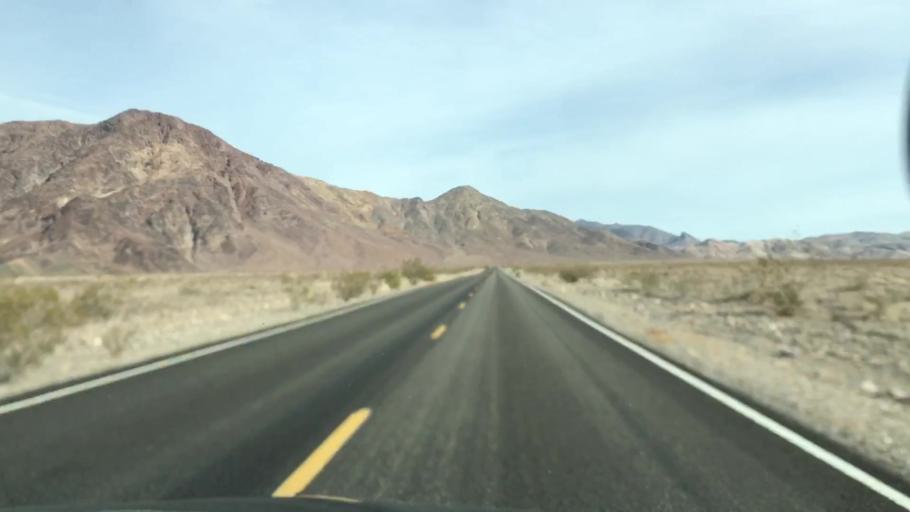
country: US
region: Nevada
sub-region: Nye County
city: Beatty
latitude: 36.6885
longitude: -117.0042
